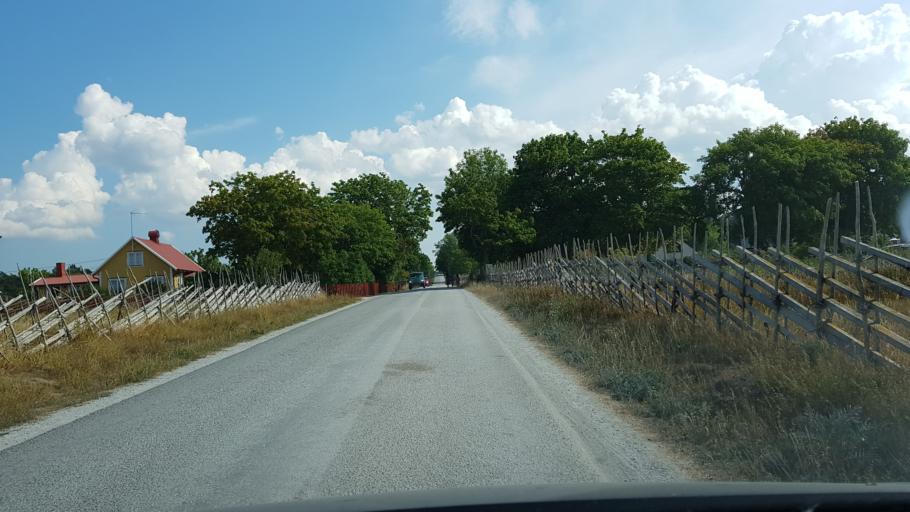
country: SE
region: Gotland
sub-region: Gotland
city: Visby
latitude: 57.8248
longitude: 18.5139
